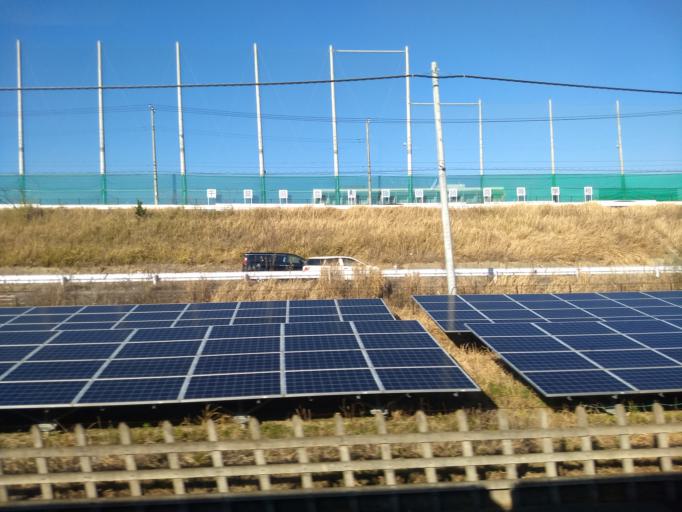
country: JP
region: Chiba
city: Shiroi
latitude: 35.8057
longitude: 140.1489
